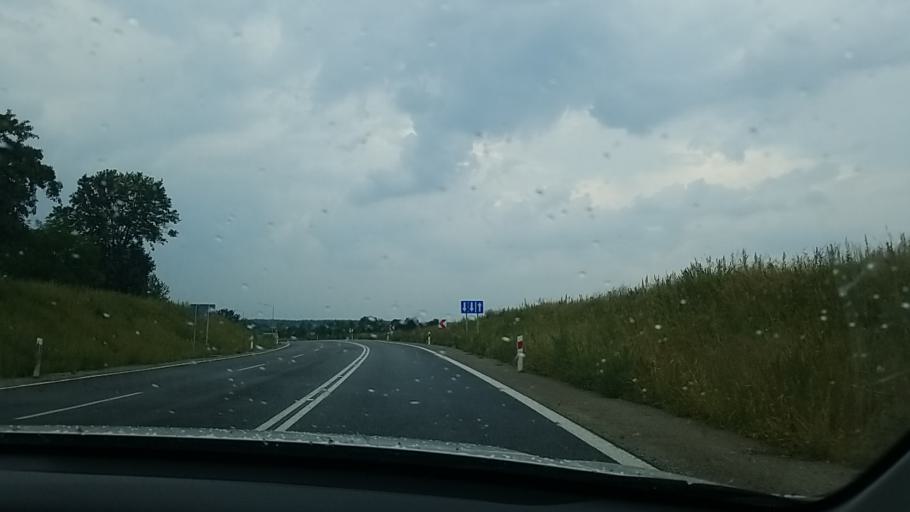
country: PL
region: Lublin Voivodeship
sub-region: Powiat lubelski
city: Krzczonow
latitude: 50.9963
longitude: 22.6793
